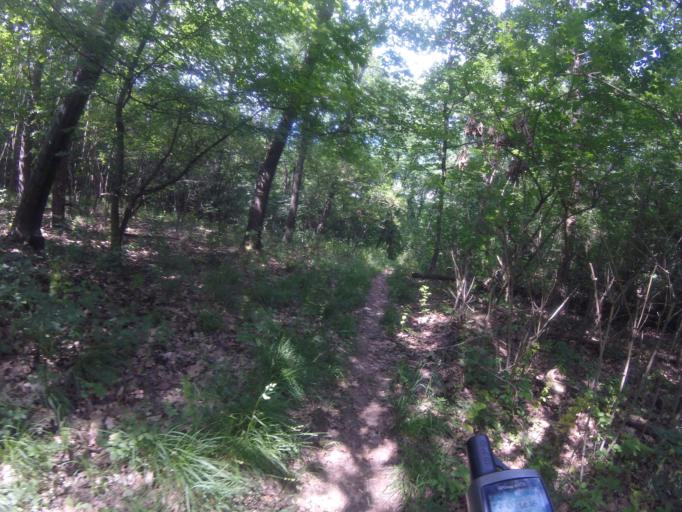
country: HU
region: Fejer
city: Szarliget
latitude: 47.4848
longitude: 18.4772
